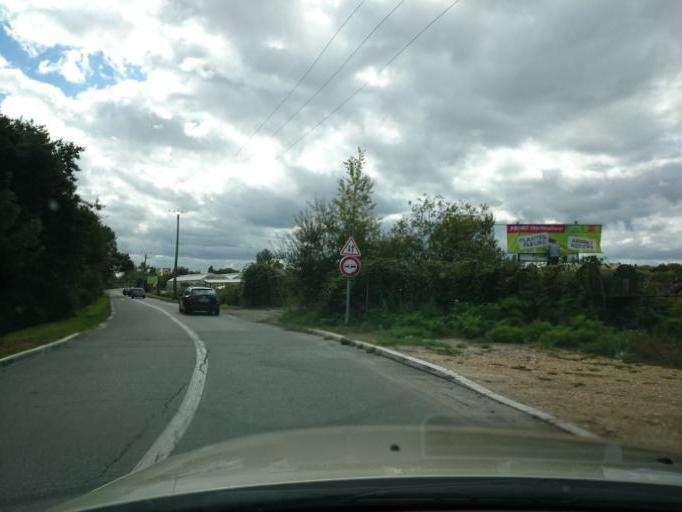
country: FR
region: Aquitaine
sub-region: Departement de la Gironde
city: Bruges
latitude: 44.8912
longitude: -0.5901
